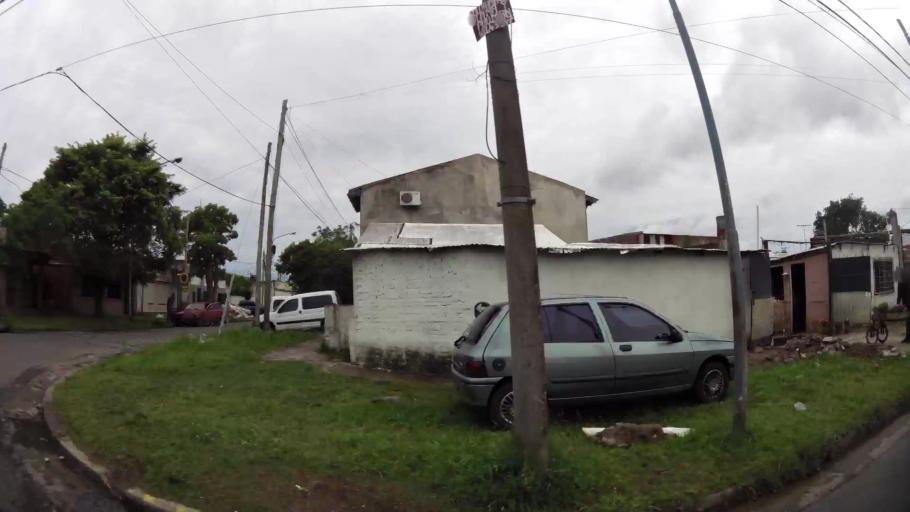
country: AR
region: Buenos Aires
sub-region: Partido de Lanus
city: Lanus
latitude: -34.7235
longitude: -58.3783
